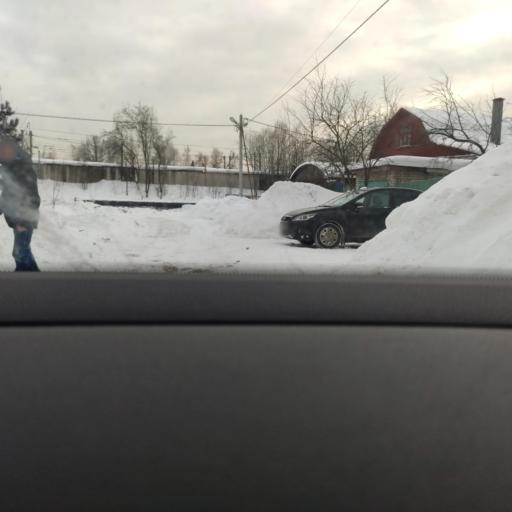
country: RU
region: Moskovskaya
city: Kokoshkino
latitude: 55.6029
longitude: 37.1746
